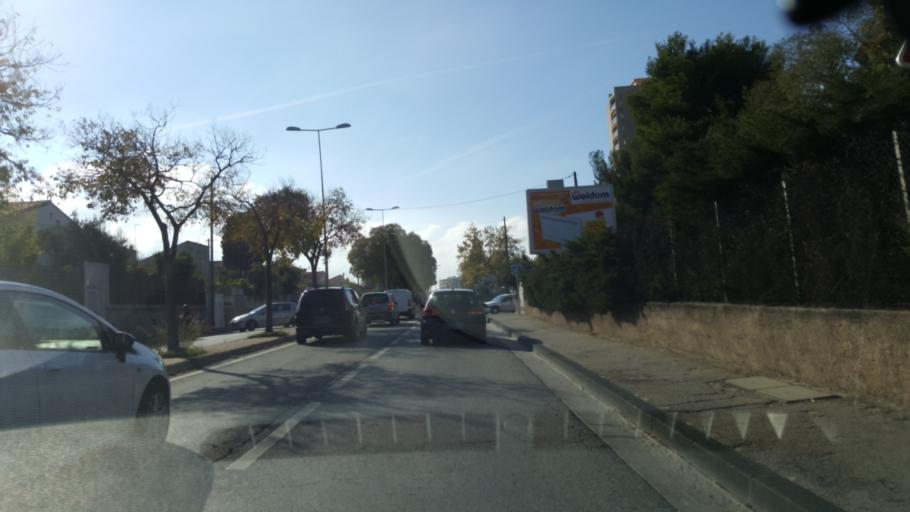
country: FR
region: Provence-Alpes-Cote d'Azur
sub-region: Departement des Bouches-du-Rhone
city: Marseille 10
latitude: 43.2712
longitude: 5.4256
